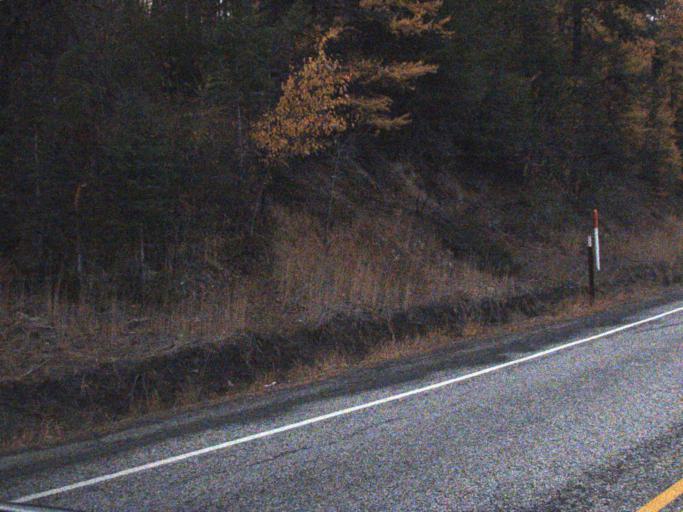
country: US
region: Washington
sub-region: Ferry County
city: Republic
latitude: 48.6061
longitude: -118.5373
